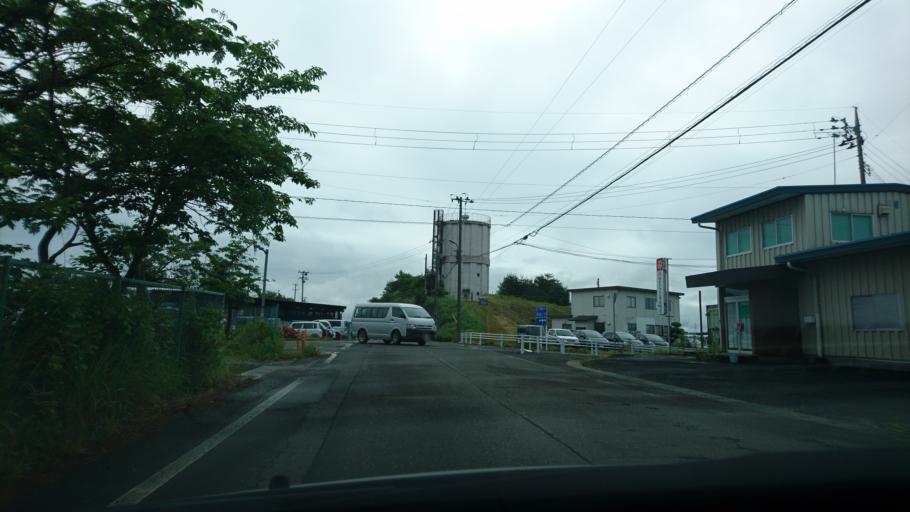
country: JP
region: Iwate
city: Ichinoseki
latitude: 38.9032
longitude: 141.1603
